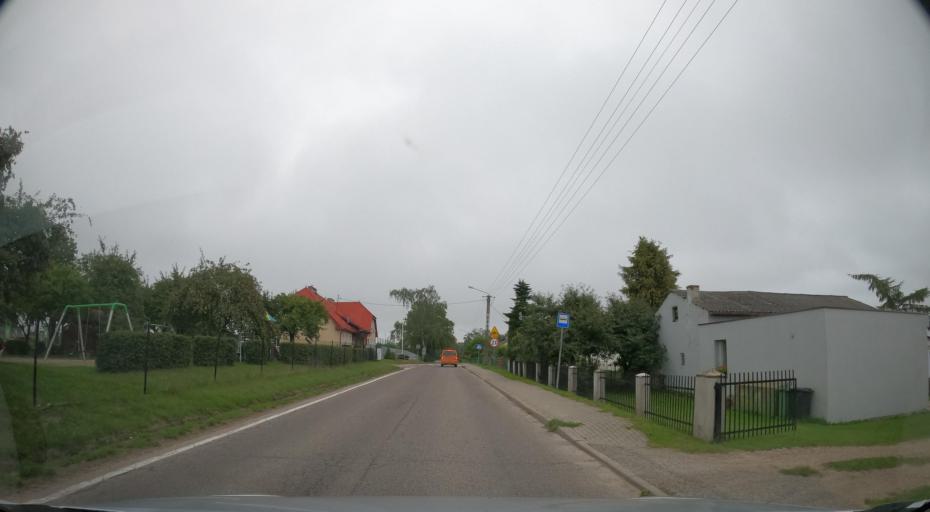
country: PL
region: Pomeranian Voivodeship
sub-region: Powiat wejherowski
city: Szemud
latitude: 54.5019
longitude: 18.1505
